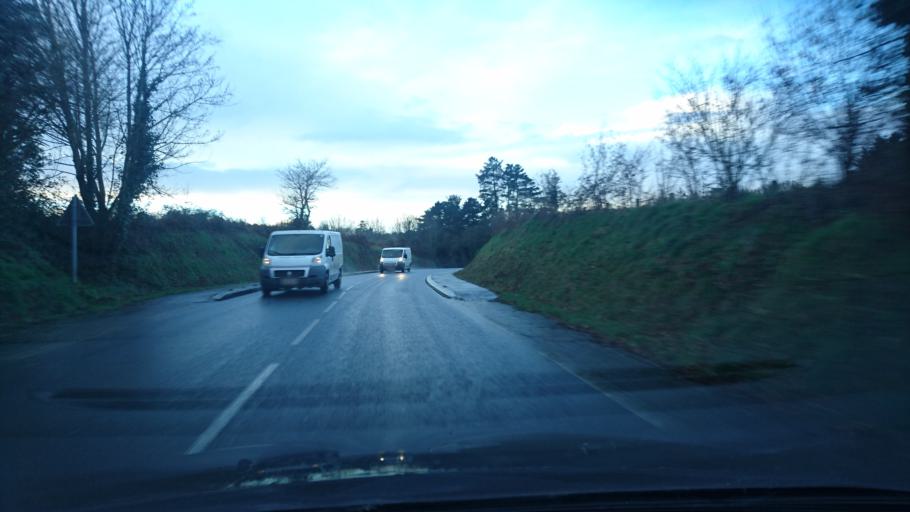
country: FR
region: Brittany
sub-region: Departement du Finistere
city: Guilers
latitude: 48.4002
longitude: -4.5404
